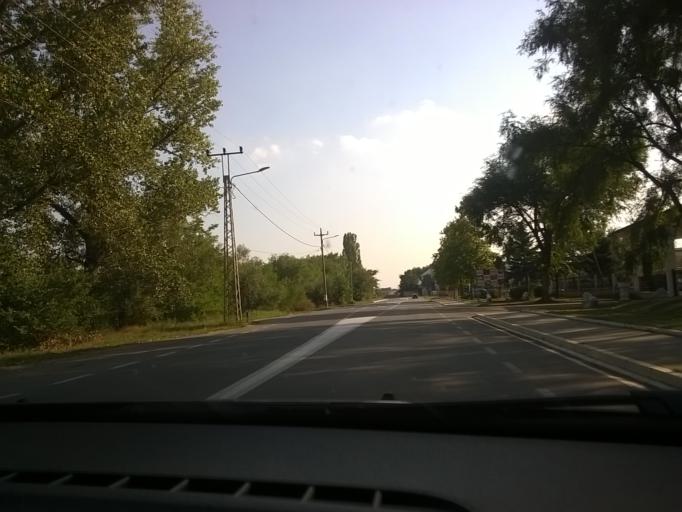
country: RS
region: Autonomna Pokrajina Vojvodina
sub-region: Juznobanatski Okrug
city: Vrsac
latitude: 45.1353
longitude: 21.2869
